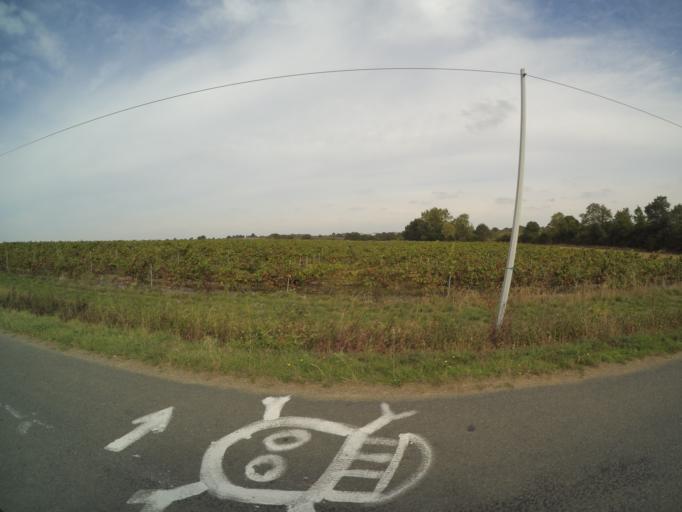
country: FR
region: Pays de la Loire
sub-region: Departement de Maine-et-Loire
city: Thouarce
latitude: 47.2109
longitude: -0.4904
